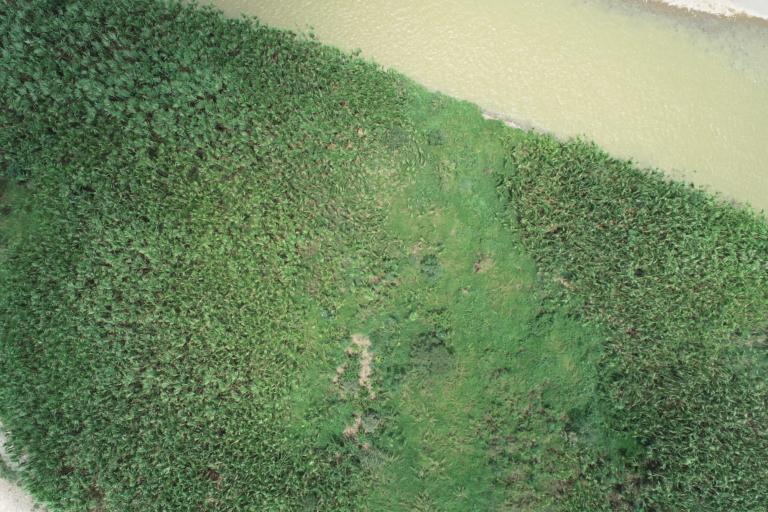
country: BO
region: La Paz
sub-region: Provincia Larecaja
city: Guanay
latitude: -15.7690
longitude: -67.6677
